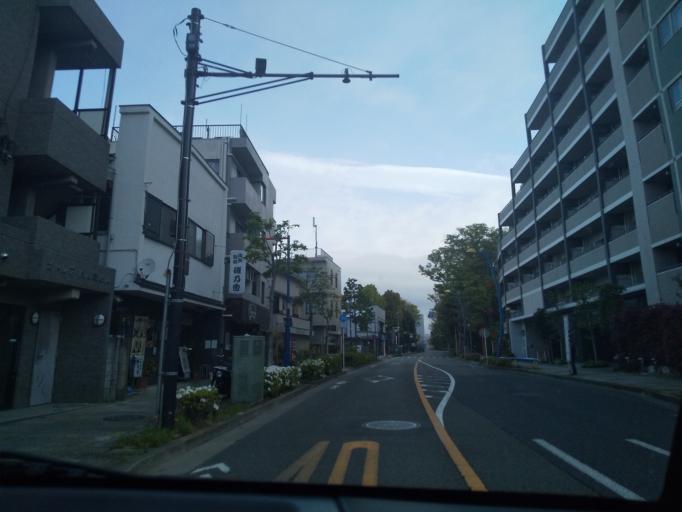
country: JP
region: Tokyo
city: Kokubunji
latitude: 35.6825
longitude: 139.4794
